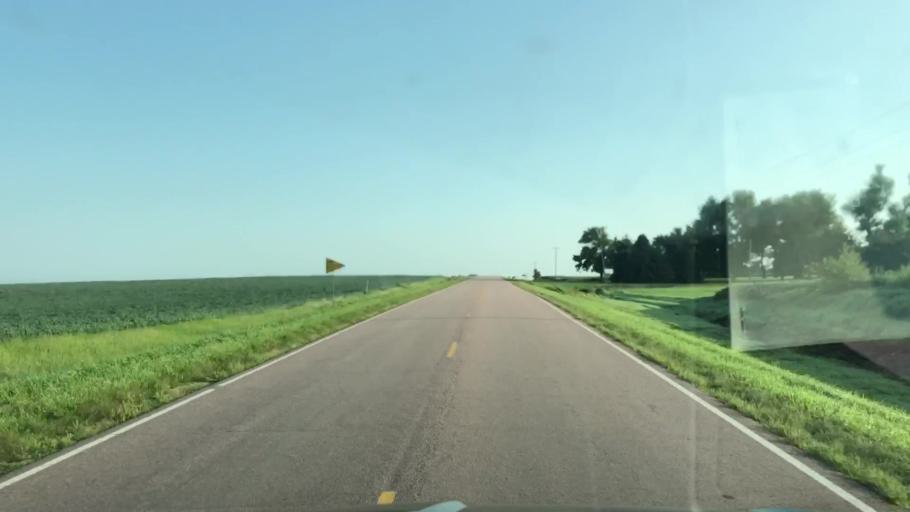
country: US
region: Iowa
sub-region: Lyon County
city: George
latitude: 43.2660
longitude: -96.0000
